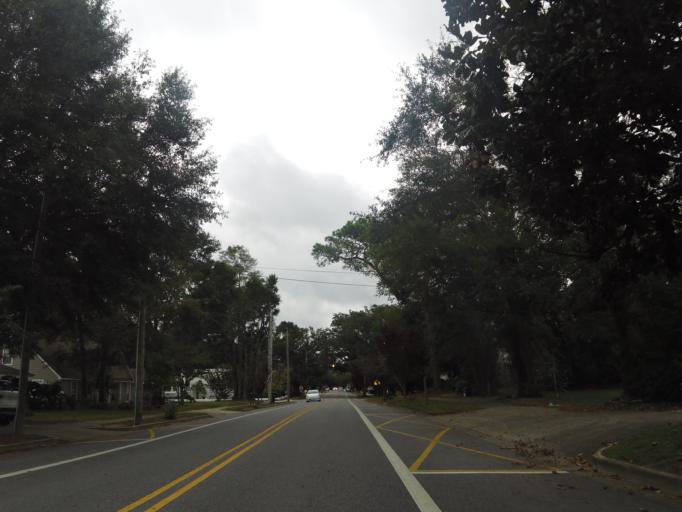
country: US
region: Alabama
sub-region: Baldwin County
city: Fairhope
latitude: 30.5190
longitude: -87.9058
